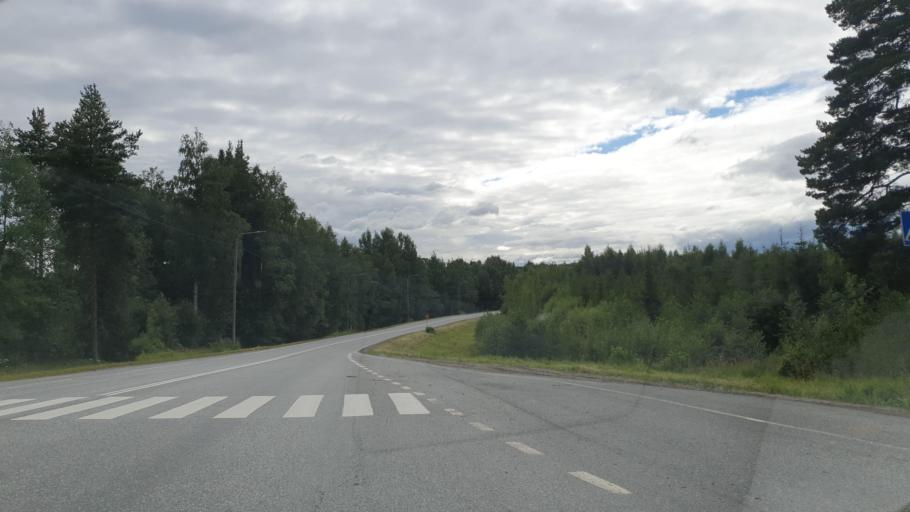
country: FI
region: Northern Savo
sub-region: Ylae-Savo
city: Iisalmi
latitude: 63.5193
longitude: 27.2378
